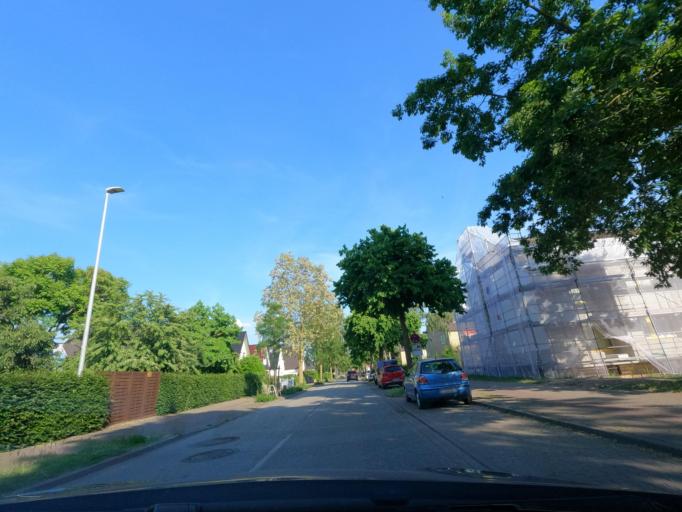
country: DE
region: Schleswig-Holstein
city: Uetersen
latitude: 53.6921
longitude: 9.6570
